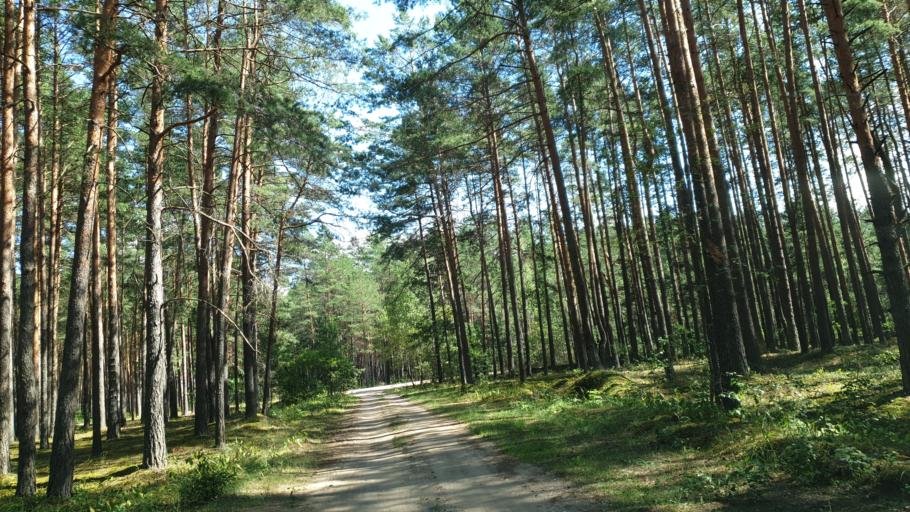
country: LT
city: Sirvintos
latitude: 54.8916
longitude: 24.9548
